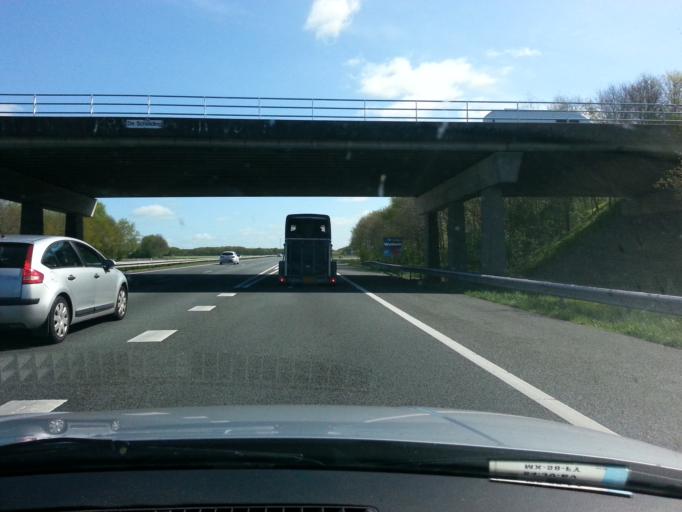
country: NL
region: Friesland
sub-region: Gemeente Smallingerland
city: Drachtstercompagnie
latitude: 53.1291
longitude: 6.1847
